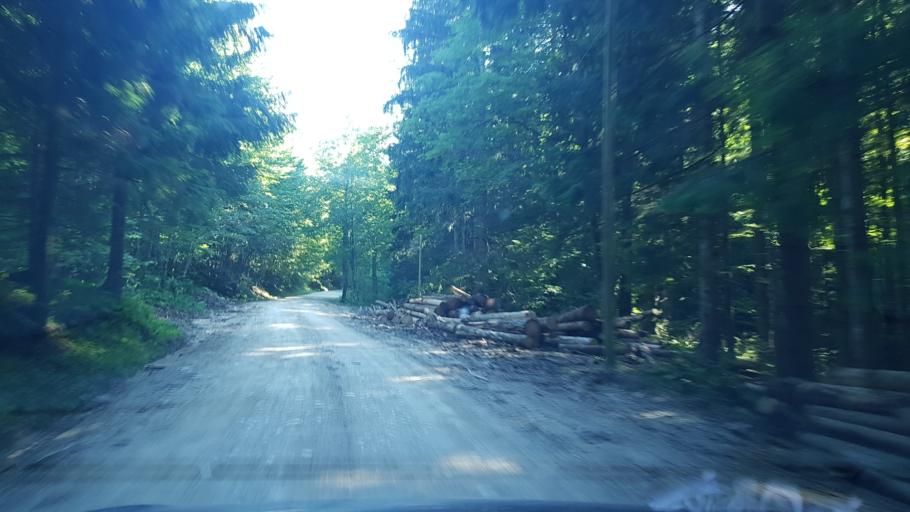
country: SI
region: Ravne na Koroskem
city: Kotlje
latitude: 46.4963
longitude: 14.9439
